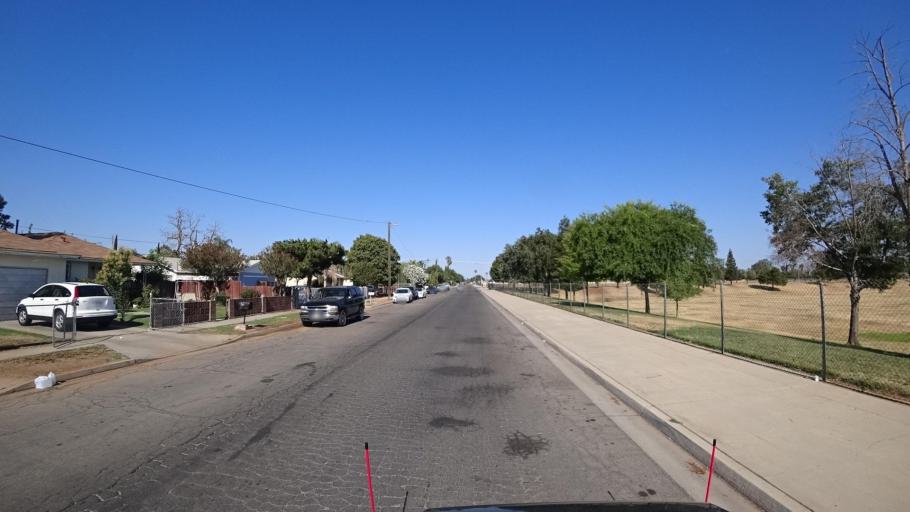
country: US
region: California
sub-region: Fresno County
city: West Park
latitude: 36.7249
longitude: -119.8248
